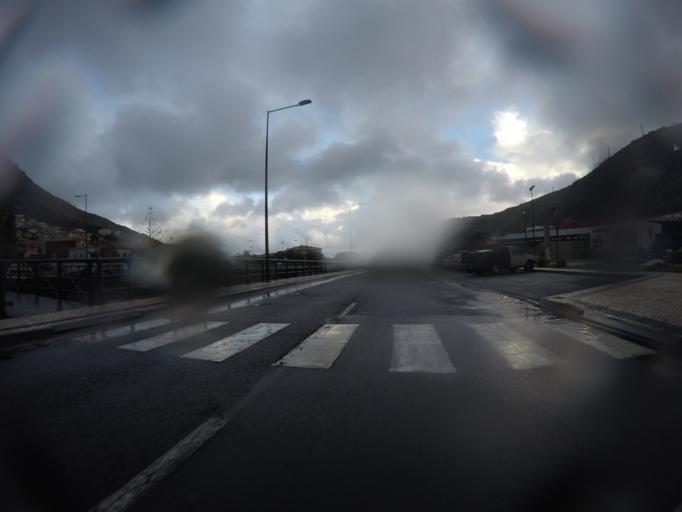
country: PT
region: Madeira
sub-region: Machico
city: Machico
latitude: 32.7217
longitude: -16.7688
